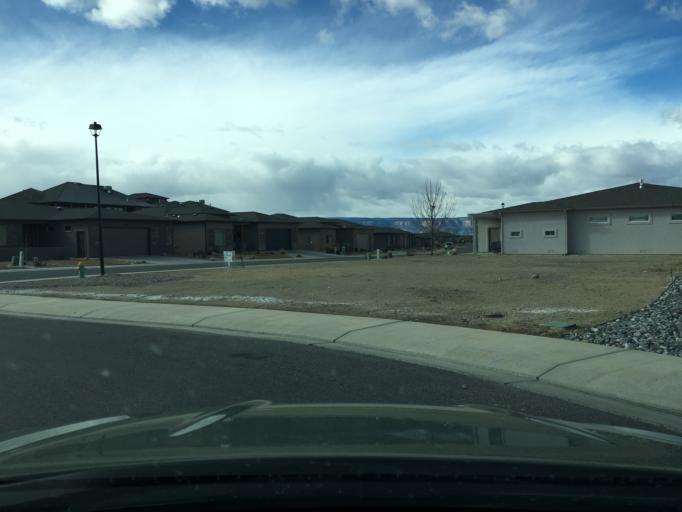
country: US
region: Colorado
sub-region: Mesa County
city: Grand Junction
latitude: 39.1321
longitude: -108.5530
